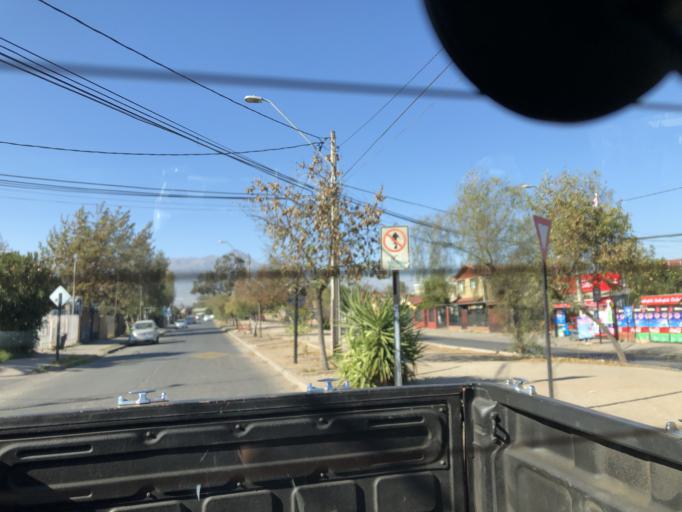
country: CL
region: Santiago Metropolitan
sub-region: Provincia de Cordillera
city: Puente Alto
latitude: -33.5788
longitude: -70.5732
